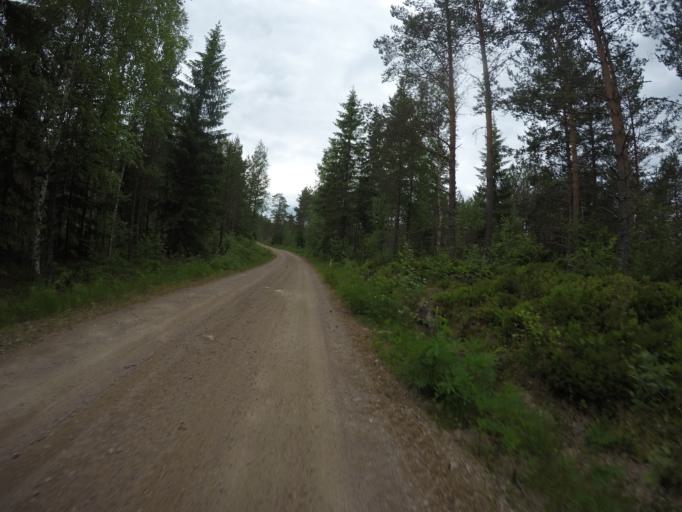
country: SE
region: Dalarna
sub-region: Ludvika Kommun
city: Abborrberget
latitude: 60.0865
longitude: 14.5510
